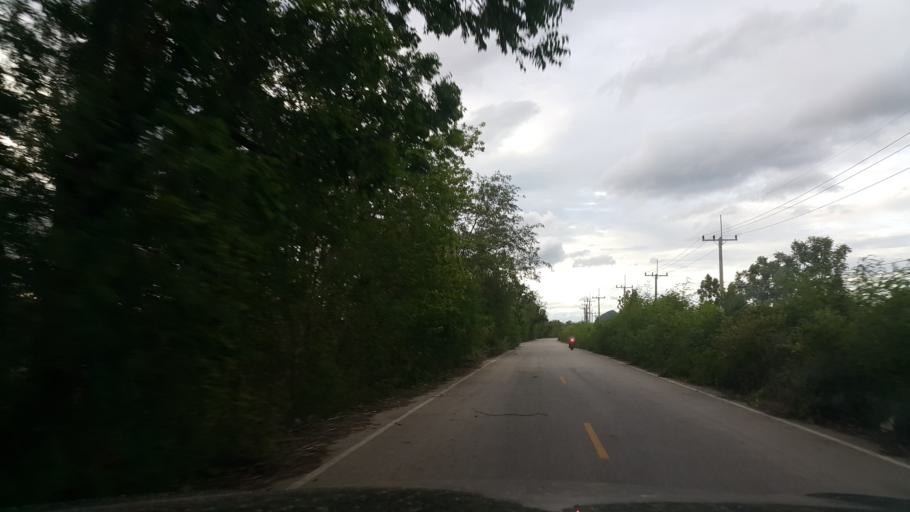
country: TH
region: Sukhothai
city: Thung Saliam
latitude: 17.1640
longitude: 99.5239
